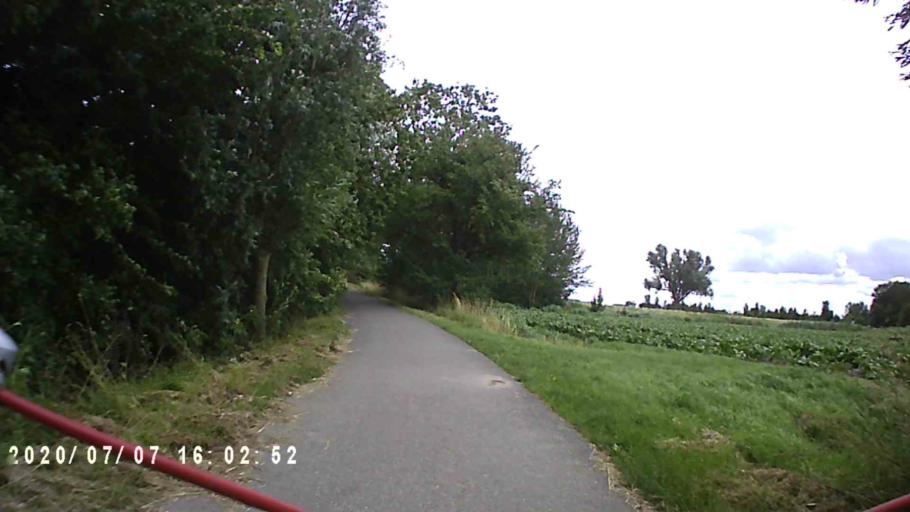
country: NL
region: Groningen
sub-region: Gemeente Winsum
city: Winsum
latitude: 53.3663
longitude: 6.5238
